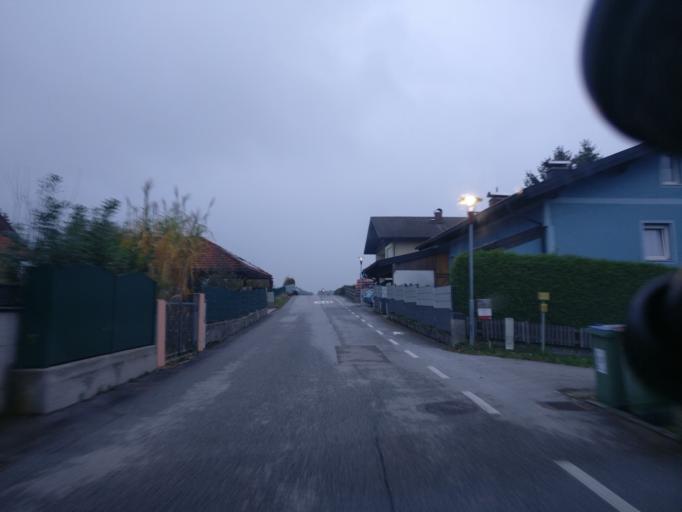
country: AT
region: Salzburg
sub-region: Politischer Bezirk Salzburg-Umgebung
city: Elixhausen
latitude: 47.8674
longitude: 13.0702
